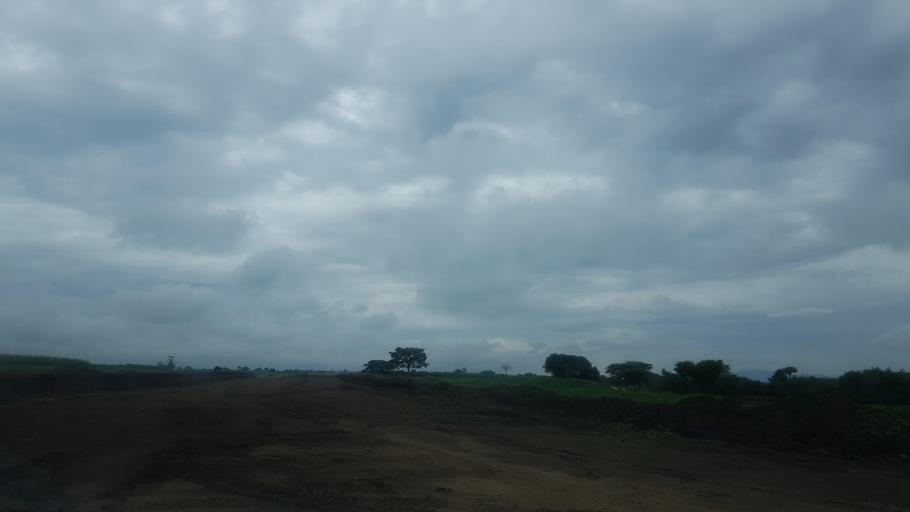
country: ET
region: Oromiya
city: Shashemene
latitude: 7.3749
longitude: 38.6465
